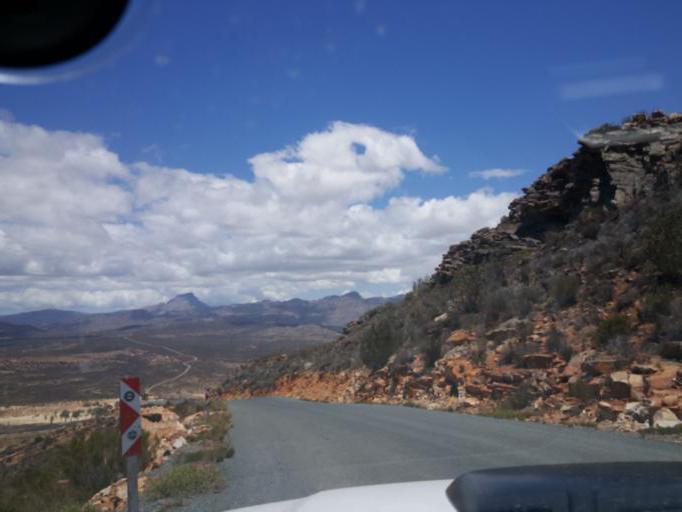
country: ZA
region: Western Cape
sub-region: Cape Winelands District Municipality
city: Ceres
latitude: -32.8979
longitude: 19.5580
